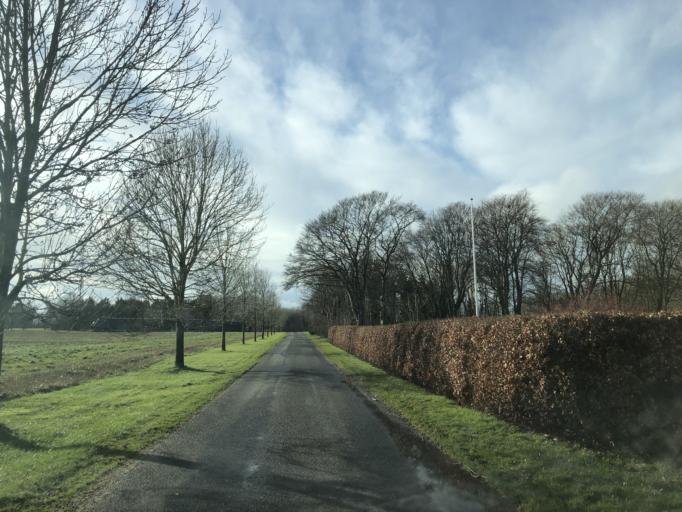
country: DK
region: North Denmark
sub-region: Vesthimmerland Kommune
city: Alestrup
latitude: 56.6405
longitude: 9.6189
